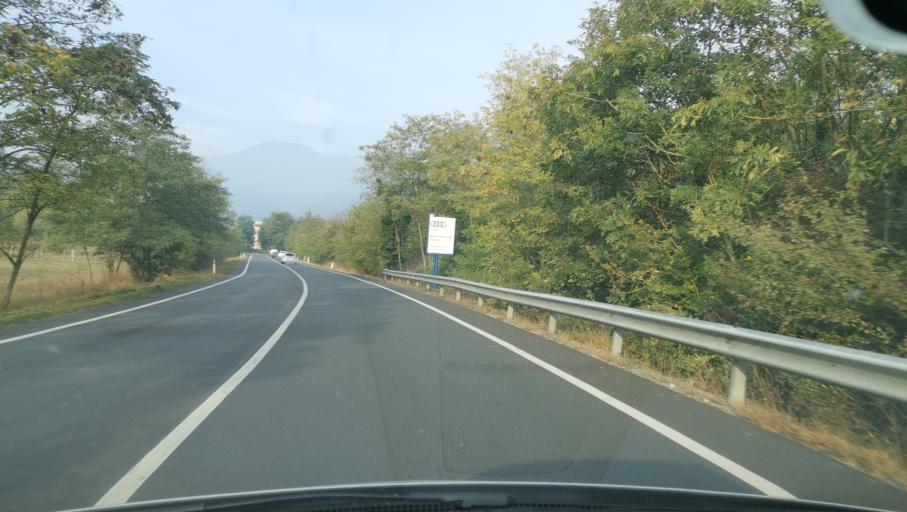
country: IT
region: Piedmont
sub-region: Provincia di Torino
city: Mattie
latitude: 45.1319
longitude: 7.1212
